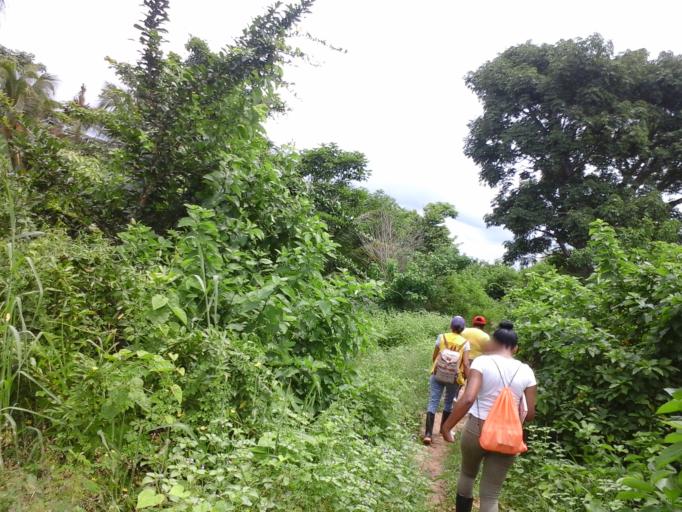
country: CO
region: Bolivar
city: San Pablo
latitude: 10.1479
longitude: -75.2765
